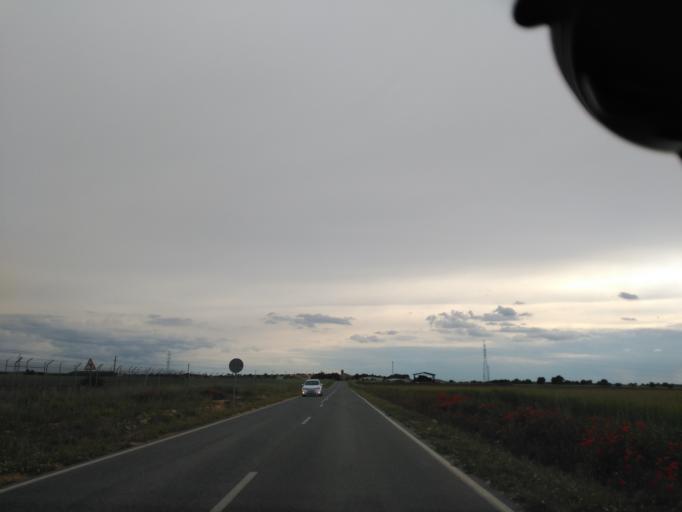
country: ES
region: Madrid
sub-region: Provincia de Madrid
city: Santorcaz
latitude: 40.4788
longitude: -3.2164
